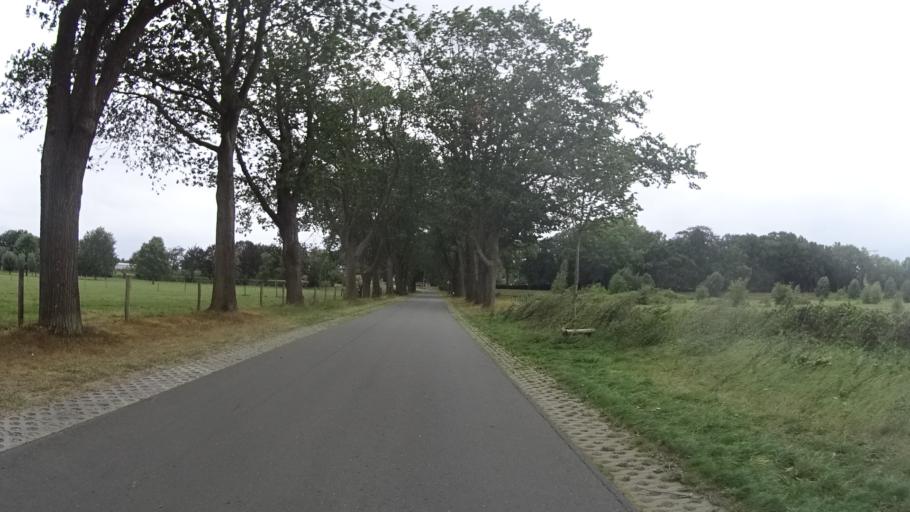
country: NL
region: Limburg
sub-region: Gemeente Venlo
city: Tegelen
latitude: 51.3399
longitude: 6.1149
